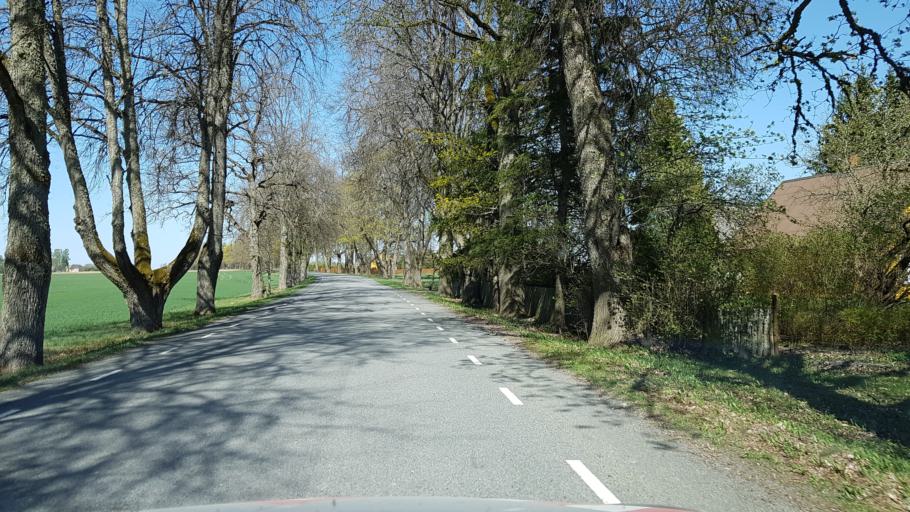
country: EE
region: Viljandimaa
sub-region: Vohma linn
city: Vohma
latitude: 58.5374
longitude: 25.5822
